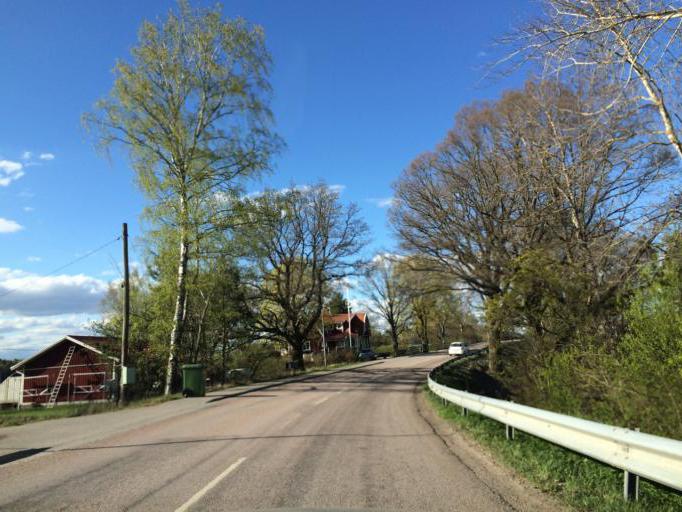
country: SE
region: Soedermanland
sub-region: Eskilstuna Kommun
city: Kvicksund
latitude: 59.4306
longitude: 16.3388
